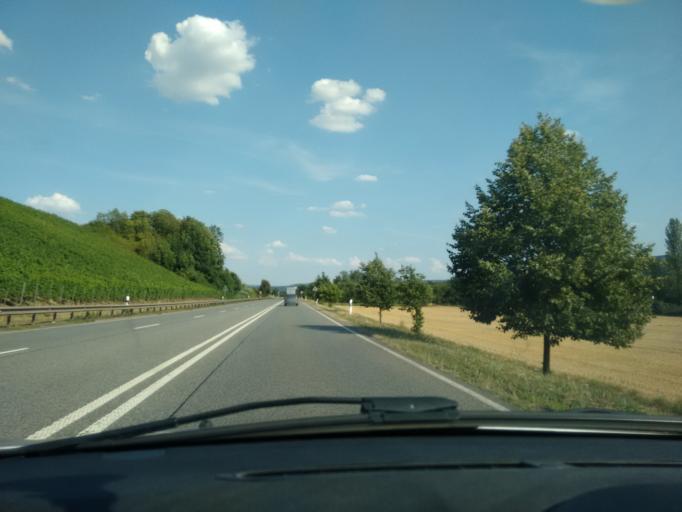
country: DE
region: Rheinland-Pfalz
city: Monzingen
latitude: 49.7993
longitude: 7.5726
